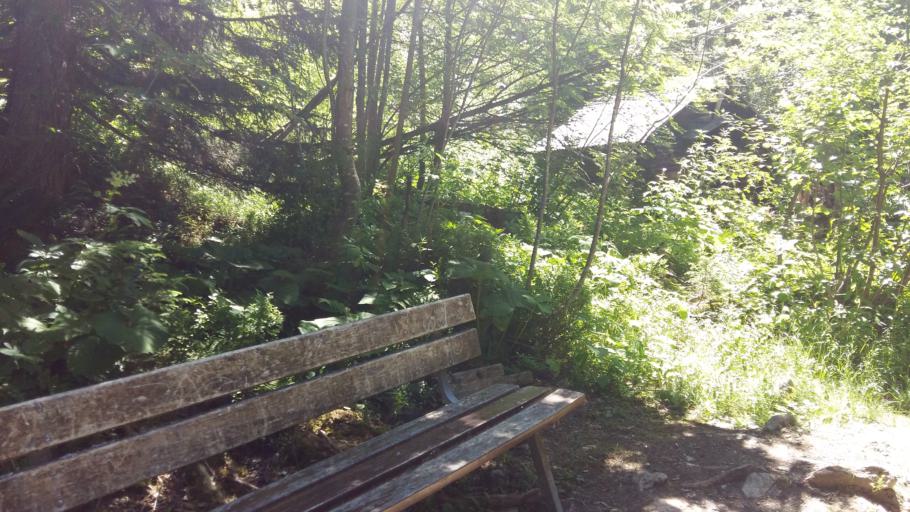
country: FR
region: Rhone-Alpes
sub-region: Departement de la Haute-Savoie
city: Les Contamines-Montjoie
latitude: 45.8015
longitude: 6.7366
